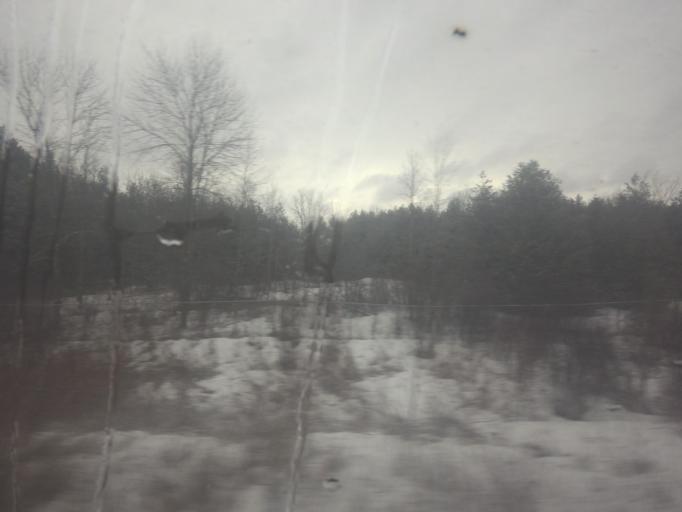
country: CA
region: Ontario
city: Bells Corners
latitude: 45.1713
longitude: -75.8324
